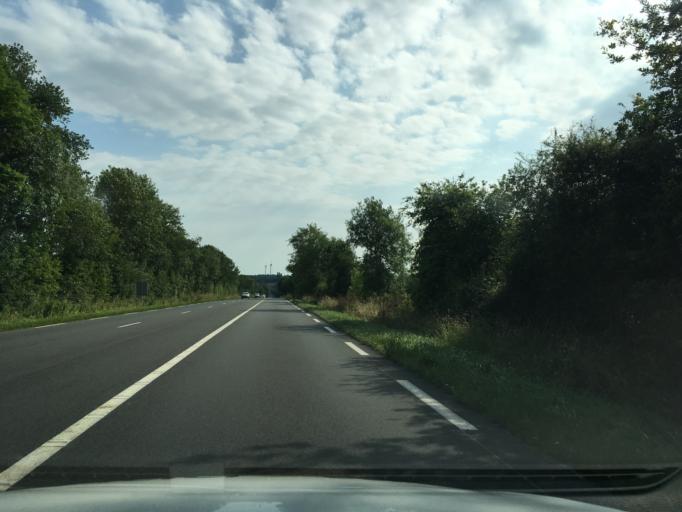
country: FR
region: Poitou-Charentes
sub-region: Departement des Deux-Sevres
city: Champdeniers-Saint-Denis
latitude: 46.4911
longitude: -0.3490
